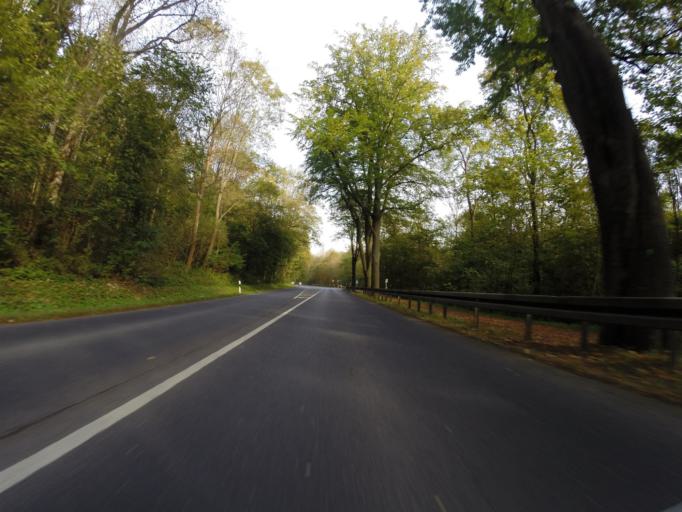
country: DE
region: Thuringia
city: Jena
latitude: 50.9397
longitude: 11.5476
